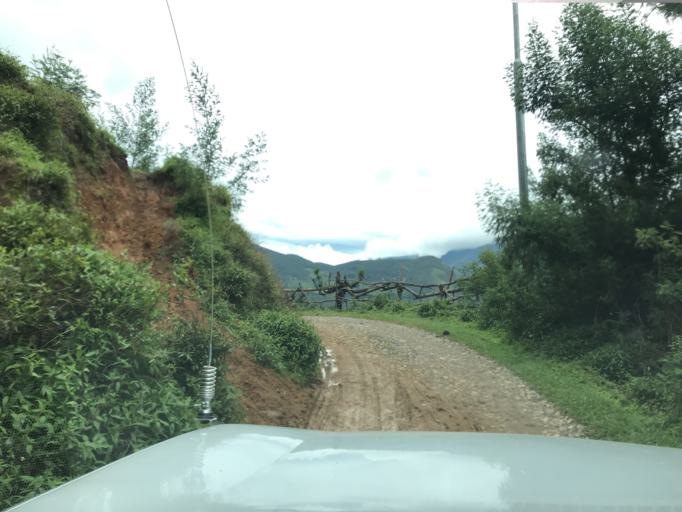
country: TL
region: Ainaro
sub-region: Ainaro
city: Ainaro
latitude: -8.8831
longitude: 125.5611
